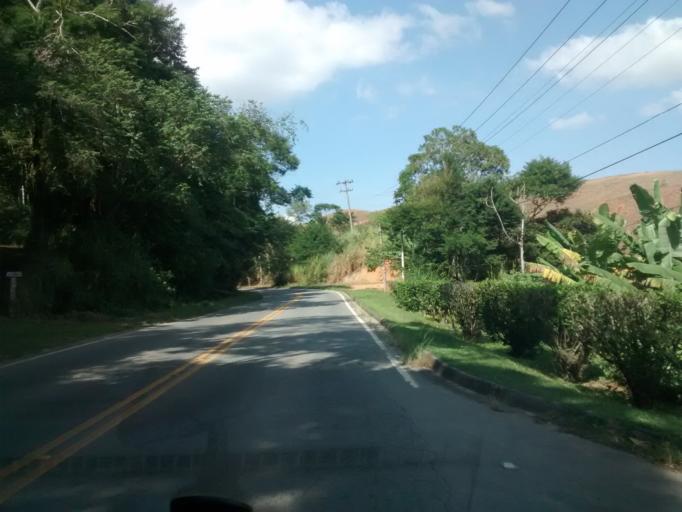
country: BR
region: Rio de Janeiro
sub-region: Miguel Pereira
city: Miguel Pereira
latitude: -22.4714
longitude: -43.5544
